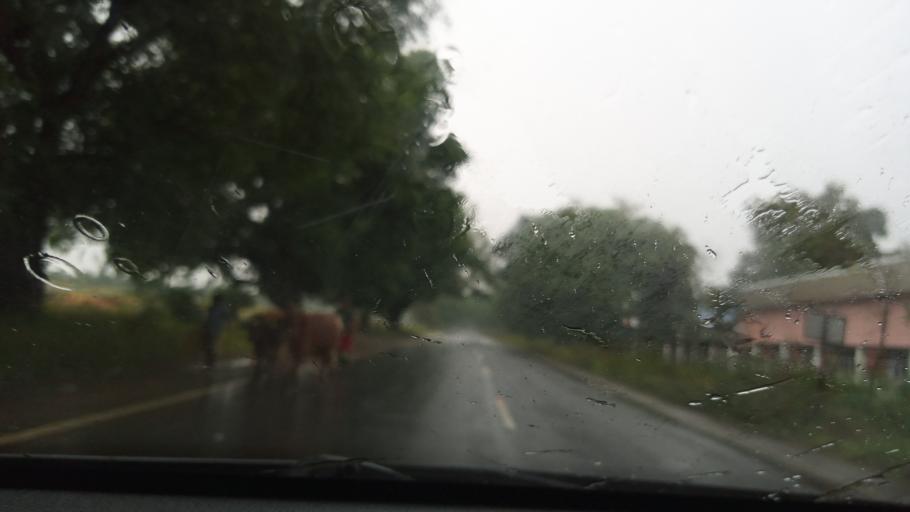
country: IN
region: Tamil Nadu
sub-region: Vellore
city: Kalavai
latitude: 12.8045
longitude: 79.4273
